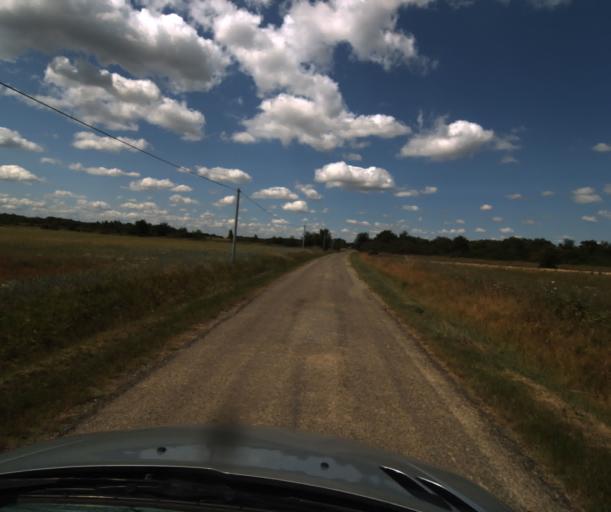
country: FR
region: Midi-Pyrenees
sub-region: Departement du Tarn-et-Garonne
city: Campsas
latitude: 43.9149
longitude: 1.2879
